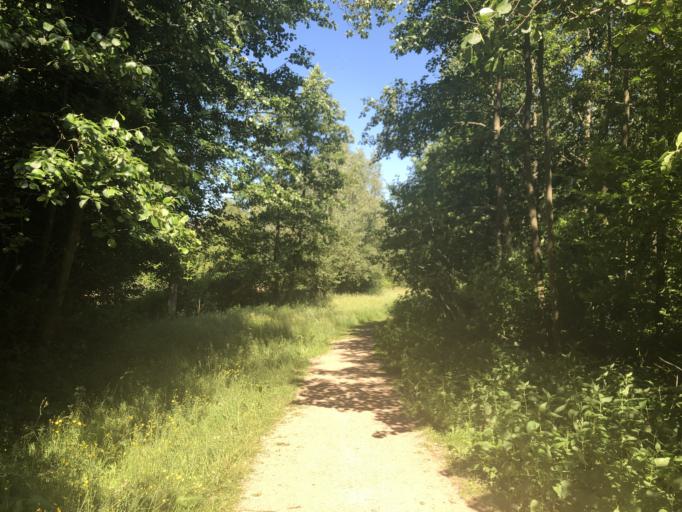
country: BE
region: Flanders
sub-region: Provincie Oost-Vlaanderen
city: Beveren
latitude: 51.1973
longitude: 4.2401
